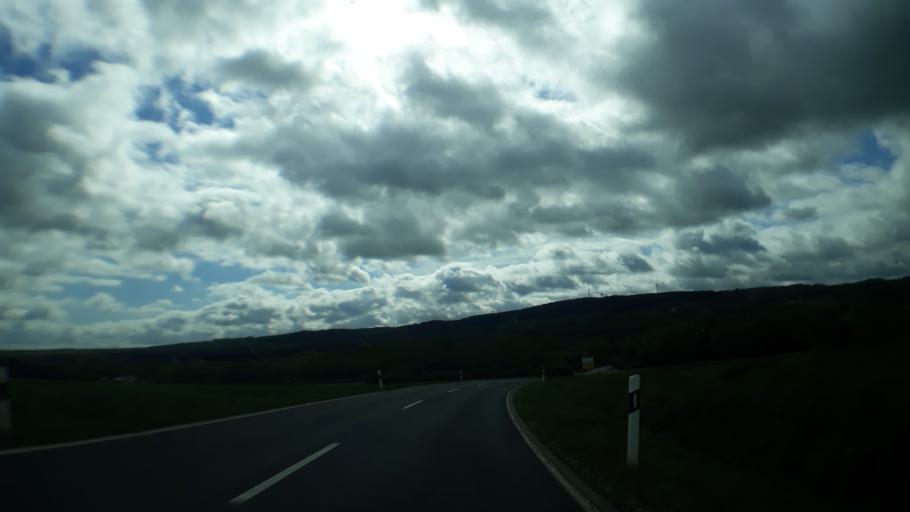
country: DE
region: North Rhine-Westphalia
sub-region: Regierungsbezirk Koln
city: Kall
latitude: 50.5805
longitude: 6.5959
